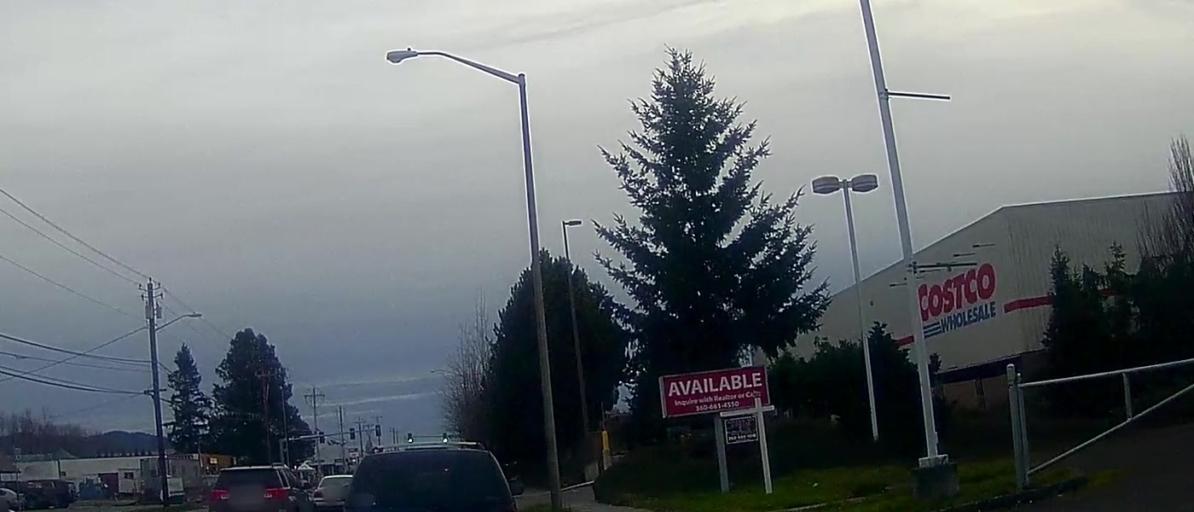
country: US
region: Washington
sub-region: Skagit County
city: Mount Vernon
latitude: 48.4317
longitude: -122.2856
